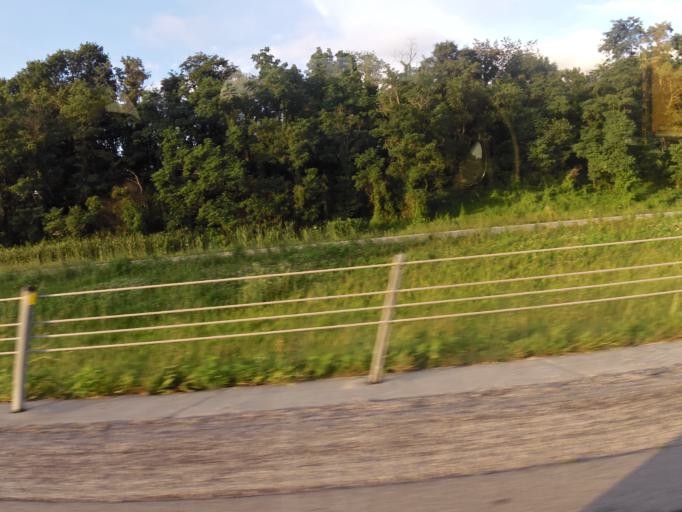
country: US
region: Kentucky
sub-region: Laurel County
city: London
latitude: 37.1708
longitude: -84.1266
